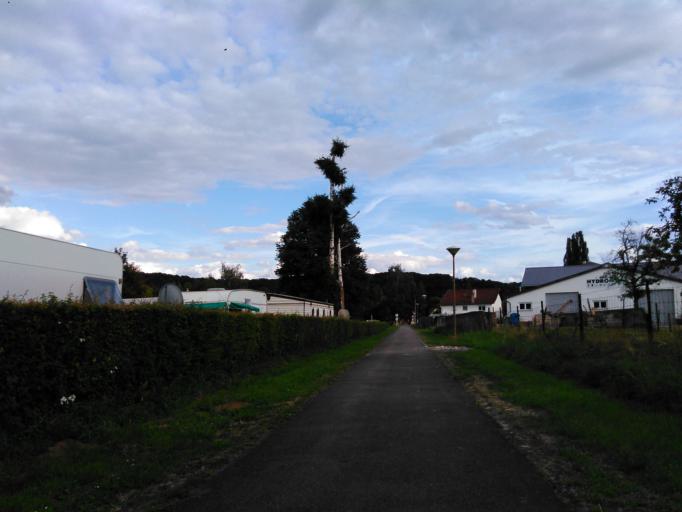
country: DE
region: Rheinland-Pfalz
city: Ralingen
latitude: 49.8082
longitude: 6.5038
